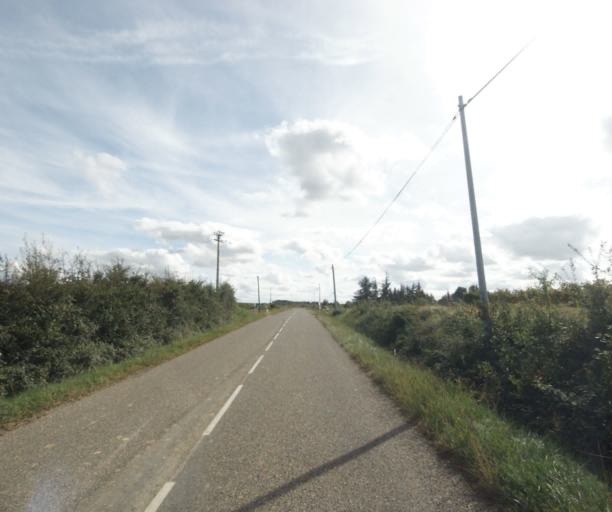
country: FR
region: Midi-Pyrenees
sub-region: Departement du Gers
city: Eauze
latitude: 43.8362
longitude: 0.1514
